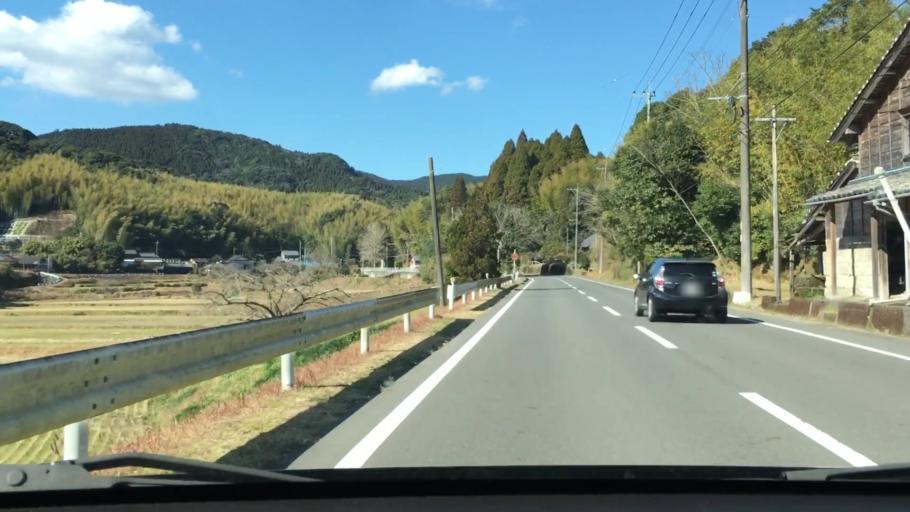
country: JP
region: Kagoshima
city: Ijuin
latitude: 31.7058
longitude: 130.4454
